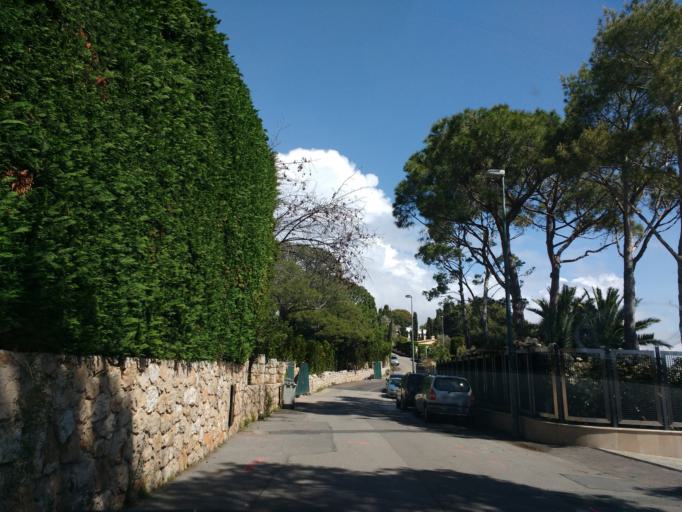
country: FR
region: Provence-Alpes-Cote d'Azur
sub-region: Departement des Alpes-Maritimes
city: Saint-Jean-Cap-Ferrat
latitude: 43.6776
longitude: 7.3333
